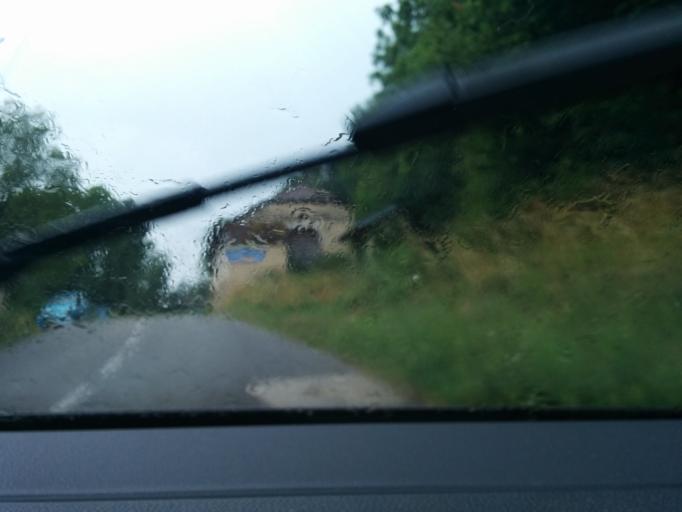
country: FR
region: Franche-Comte
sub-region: Departement du Jura
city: Saint-Lupicin
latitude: 46.4159
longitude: 5.7969
